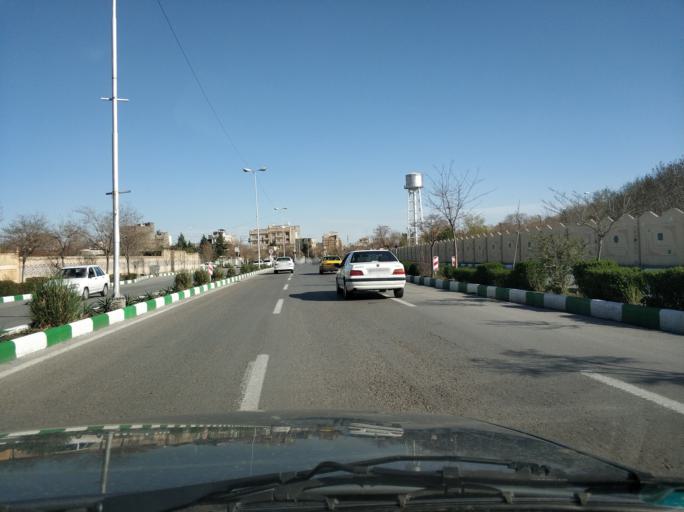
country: IR
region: Razavi Khorasan
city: Mashhad
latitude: 36.3024
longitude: 59.6300
